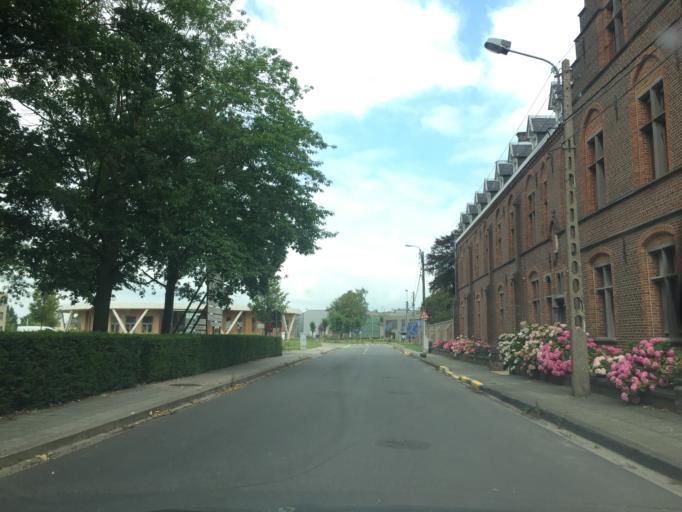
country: BE
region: Flanders
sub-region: Provincie West-Vlaanderen
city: Kortemark
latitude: 51.0305
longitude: 3.0416
